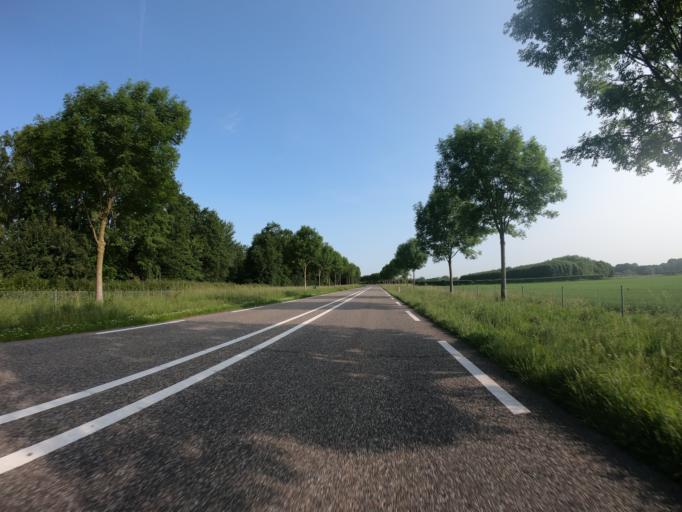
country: NL
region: North Brabant
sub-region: Gemeente Landerd
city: Reek
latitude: 51.7816
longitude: 5.6653
